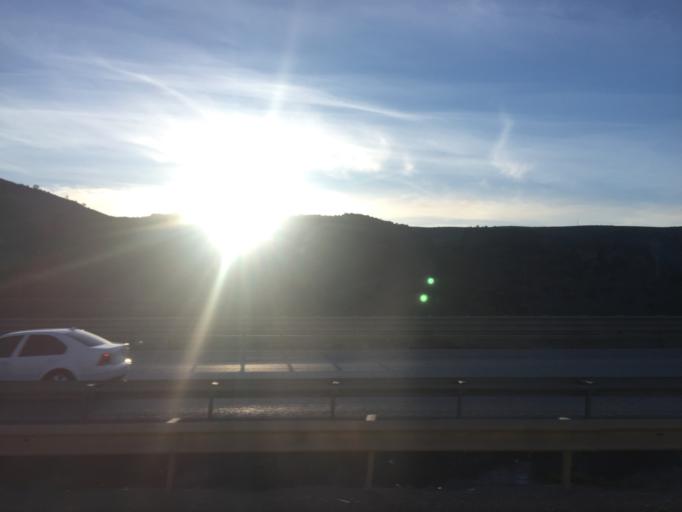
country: TR
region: Kirikkale
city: Yahsihan
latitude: 39.9329
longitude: 33.4216
